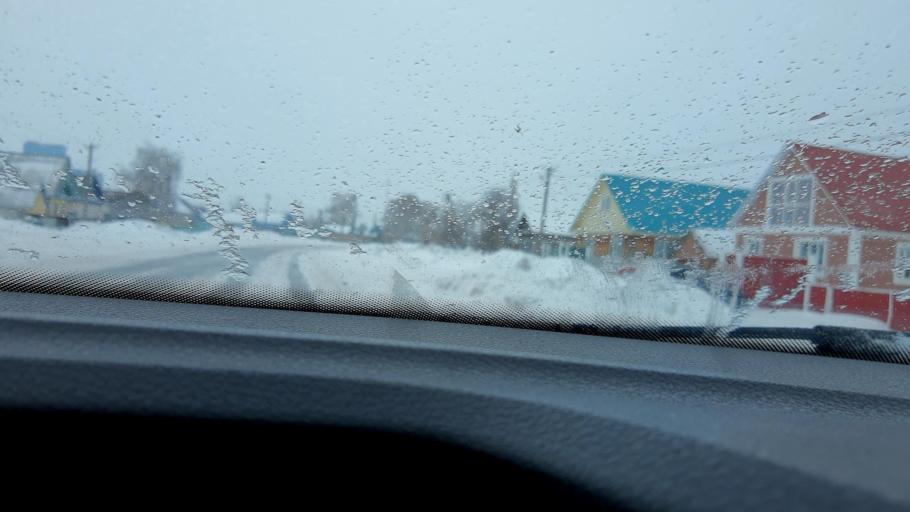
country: RU
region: Bashkortostan
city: Zirgan
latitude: 53.2320
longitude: 55.9158
